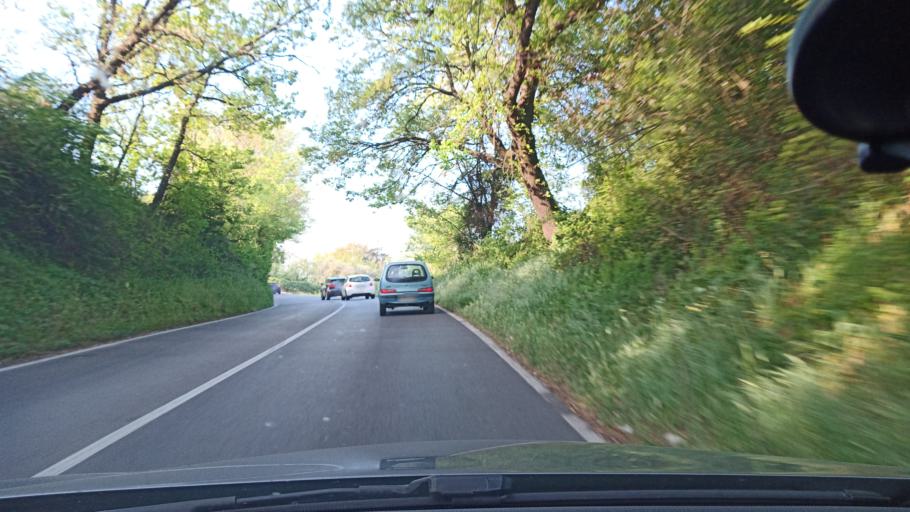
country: IT
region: Latium
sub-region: Citta metropolitana di Roma Capitale
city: Fiano Romano
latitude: 42.1843
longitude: 12.6368
